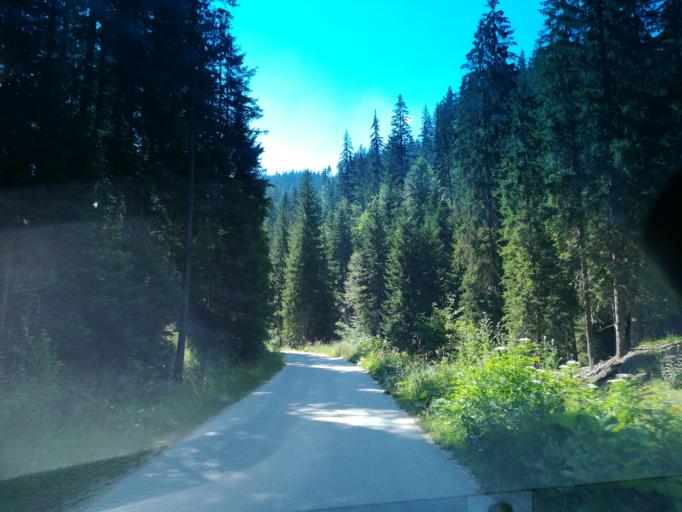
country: BG
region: Smolyan
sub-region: Obshtina Smolyan
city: Smolyan
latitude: 41.6609
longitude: 24.8054
